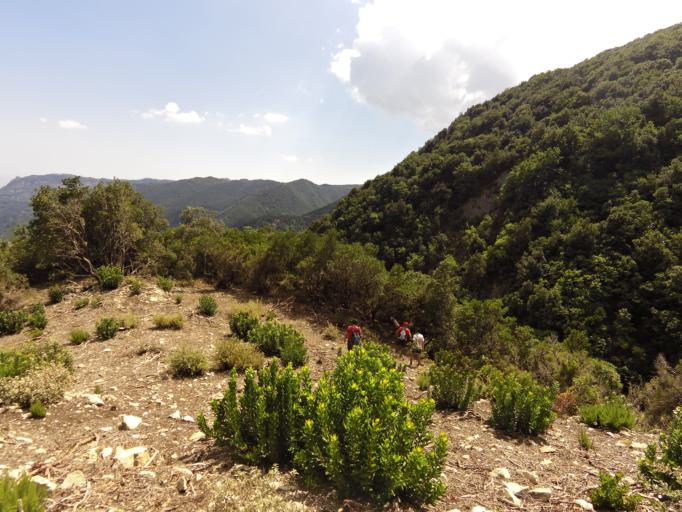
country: IT
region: Calabria
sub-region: Provincia di Vibo-Valentia
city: Nardodipace
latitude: 38.5029
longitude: 16.3955
